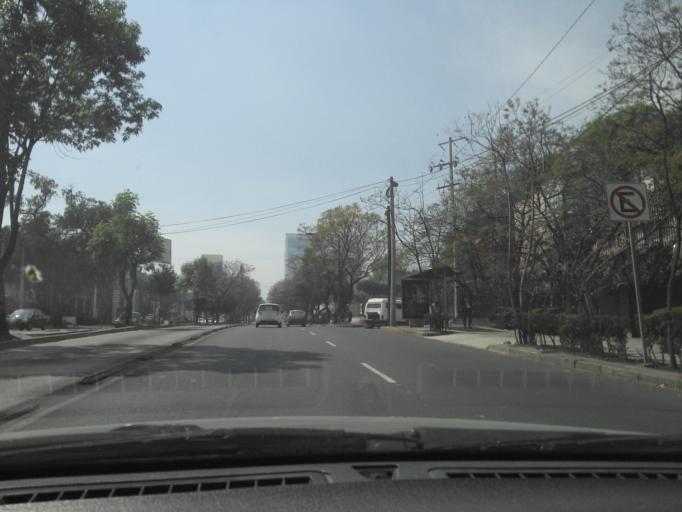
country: MX
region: Mexico City
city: Alvaro Obregon
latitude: 19.3456
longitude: -99.1882
